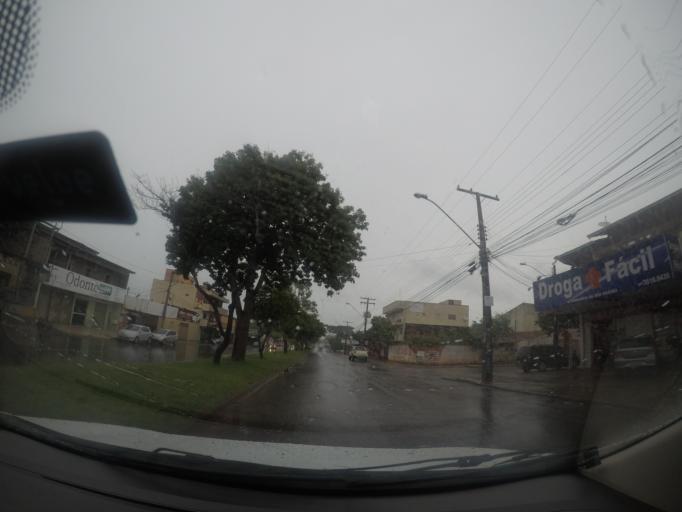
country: BR
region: Goias
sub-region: Goiania
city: Goiania
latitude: -16.6278
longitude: -49.3311
